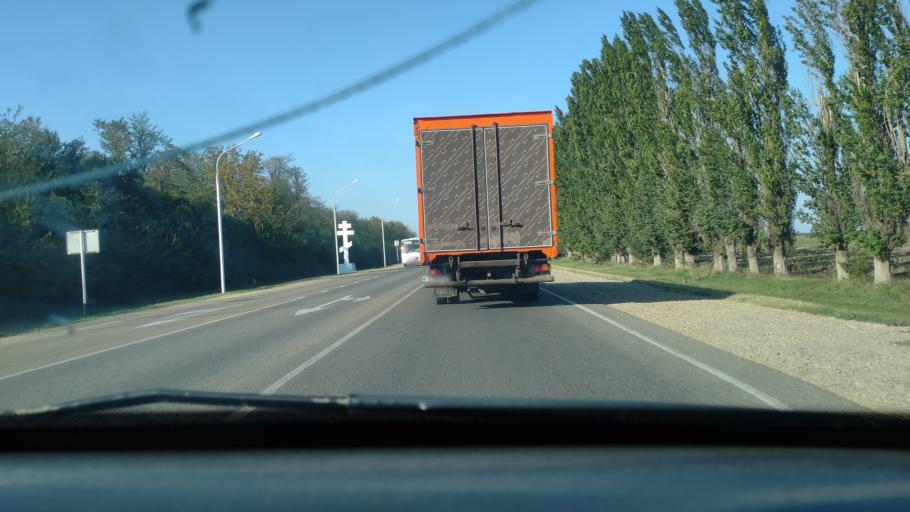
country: RU
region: Krasnodarskiy
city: Novotitarovskaya
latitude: 45.2612
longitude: 38.9996
